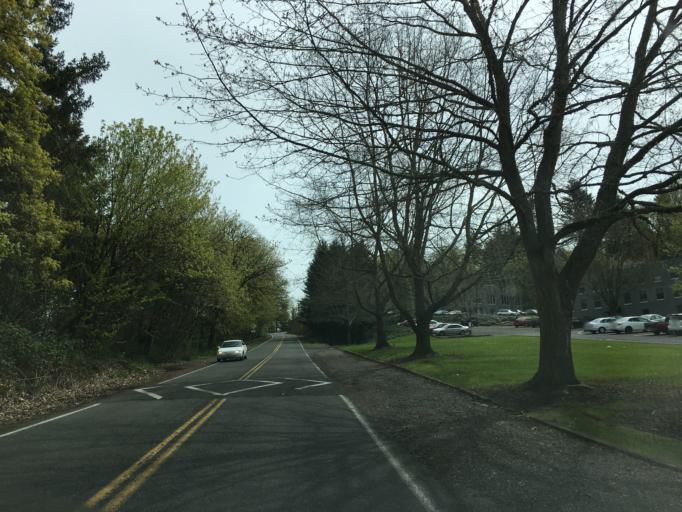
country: US
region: Oregon
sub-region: Multnomah County
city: Lents
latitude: 45.5509
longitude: -122.5655
